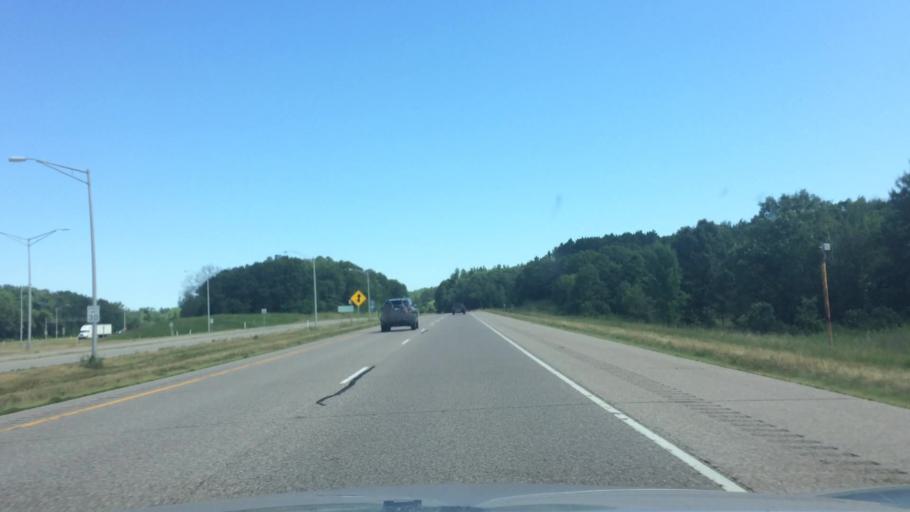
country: US
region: Wisconsin
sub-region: Marquette County
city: Westfield
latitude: 44.0768
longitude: -89.5346
